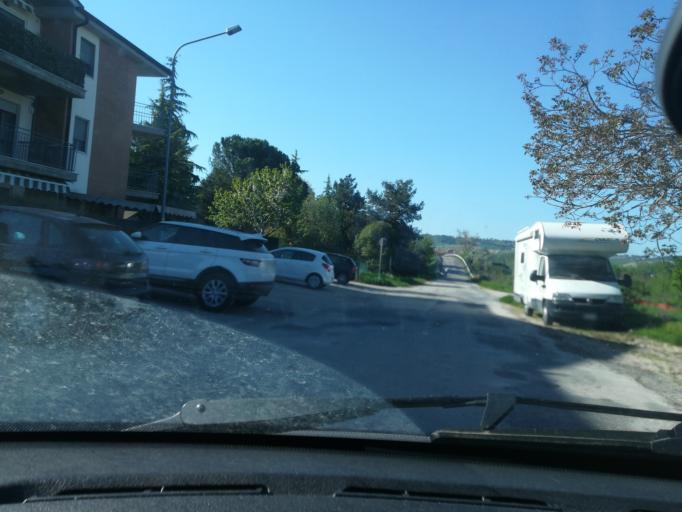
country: IT
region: The Marches
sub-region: Provincia di Macerata
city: Zona Industriale
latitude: 43.2658
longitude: 13.4938
